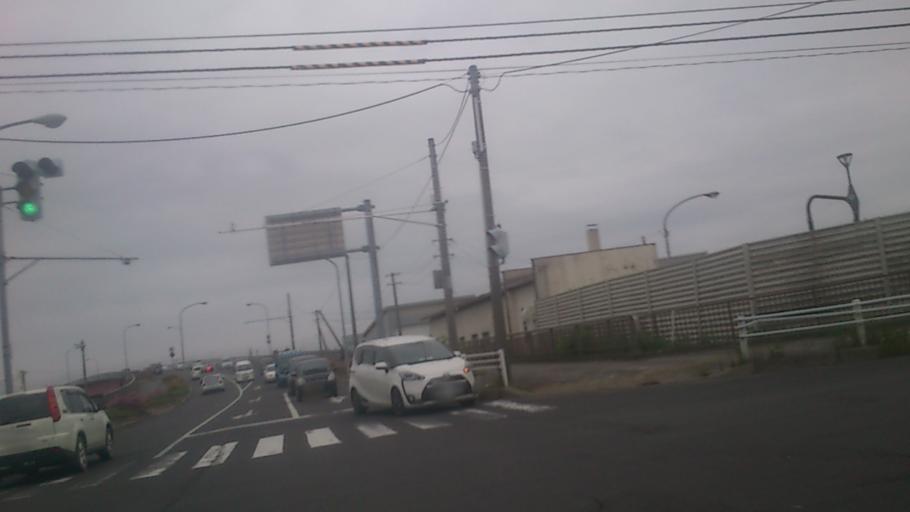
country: JP
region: Hokkaido
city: Kushiro
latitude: 42.9975
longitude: 144.4106
